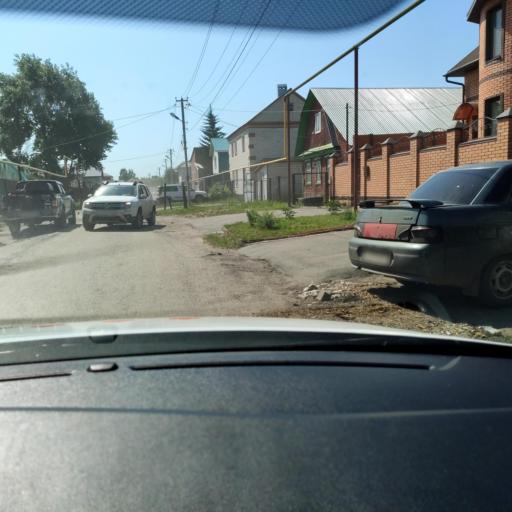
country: RU
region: Tatarstan
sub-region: Gorod Kazan'
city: Kazan
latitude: 55.8218
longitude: 49.1992
